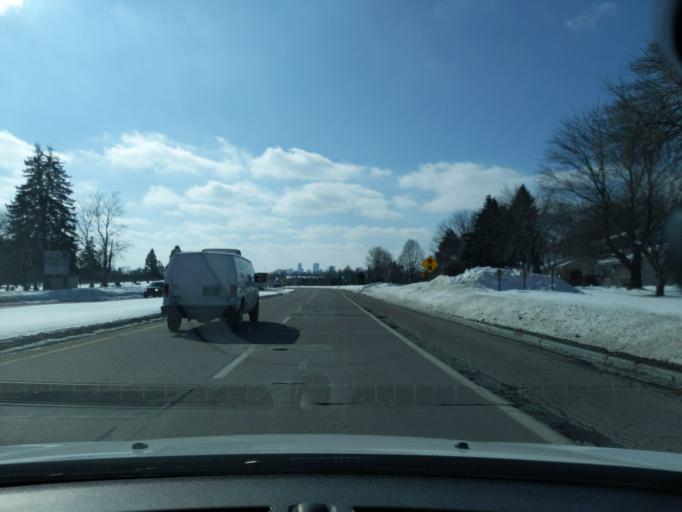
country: US
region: Minnesota
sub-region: Hennepin County
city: Saint Anthony
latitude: 45.0190
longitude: -93.2149
